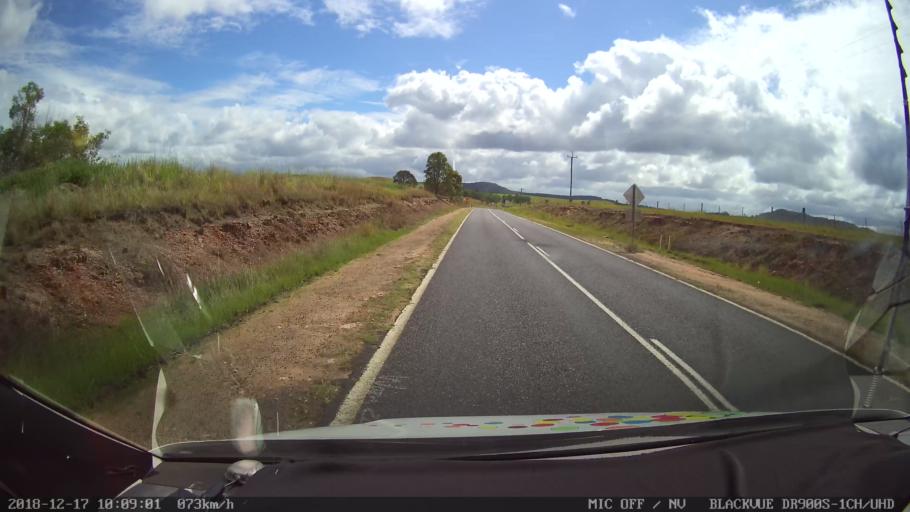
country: AU
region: New South Wales
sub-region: Tenterfield Municipality
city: Carrolls Creek
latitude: -28.8886
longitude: 152.5384
